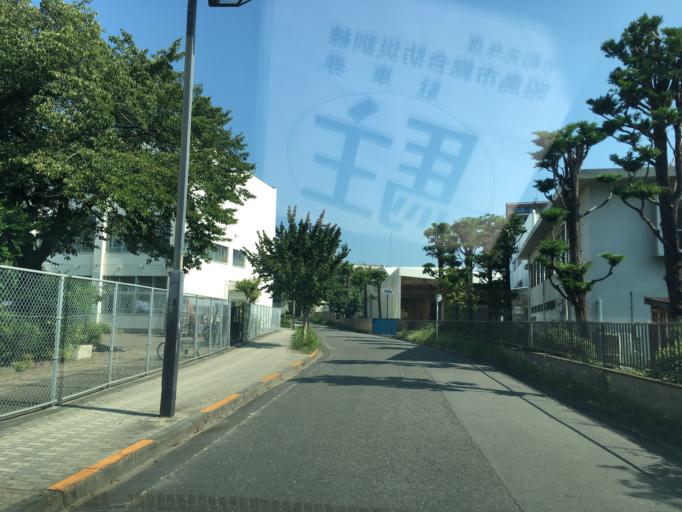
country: JP
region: Tokyo
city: Fussa
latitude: 35.7162
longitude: 139.3447
